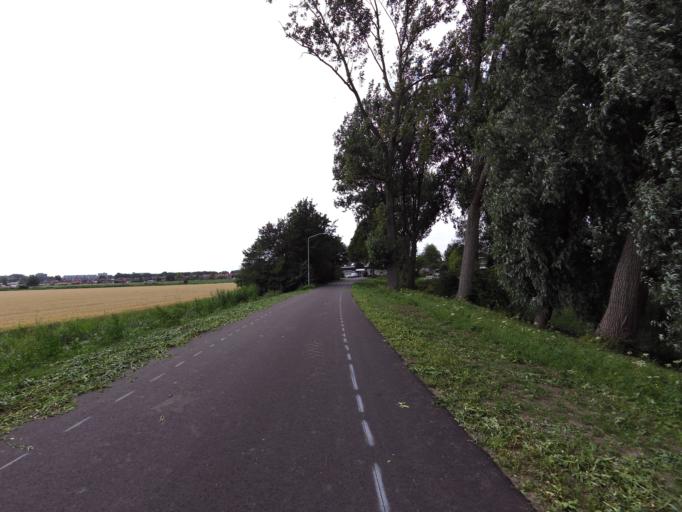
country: NL
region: South Holland
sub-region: Gemeente Dordrecht
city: Dordrecht
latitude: 51.7882
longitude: 4.7021
